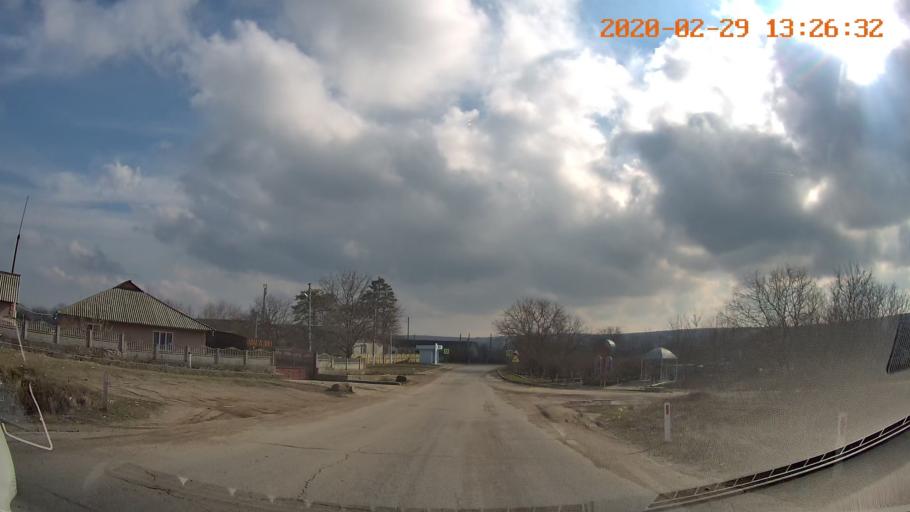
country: MD
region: Telenesti
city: Camenca
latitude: 47.9193
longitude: 28.6379
